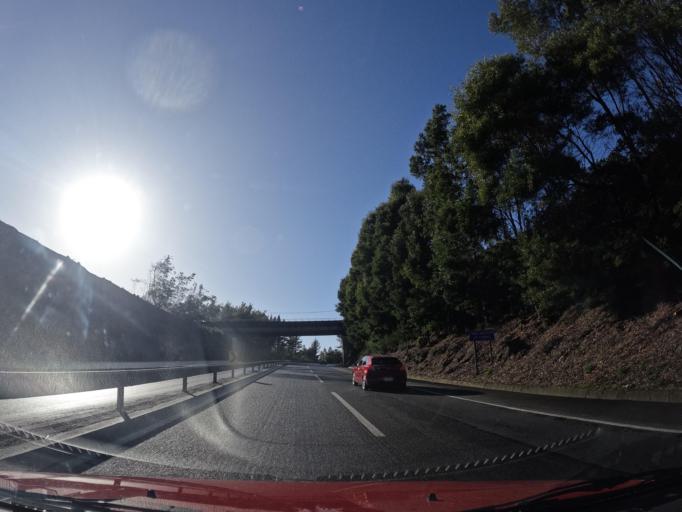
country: CL
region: Biobio
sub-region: Provincia de Concepcion
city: Penco
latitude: -36.7601
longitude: -72.9363
